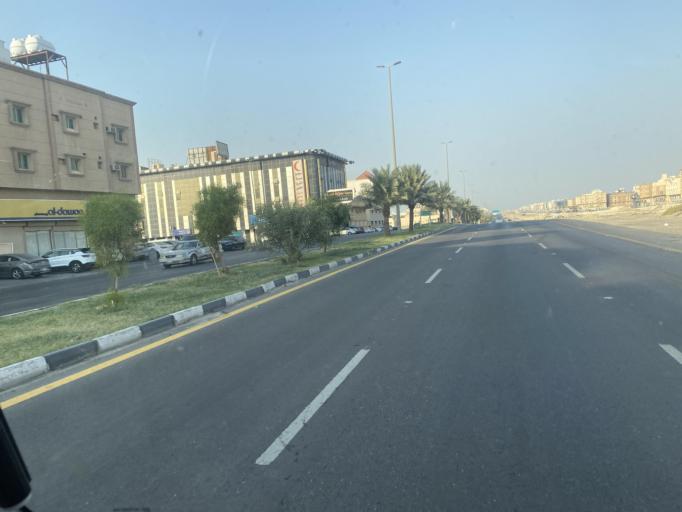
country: SA
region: Eastern Province
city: Dammam
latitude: 26.3595
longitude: 50.0656
